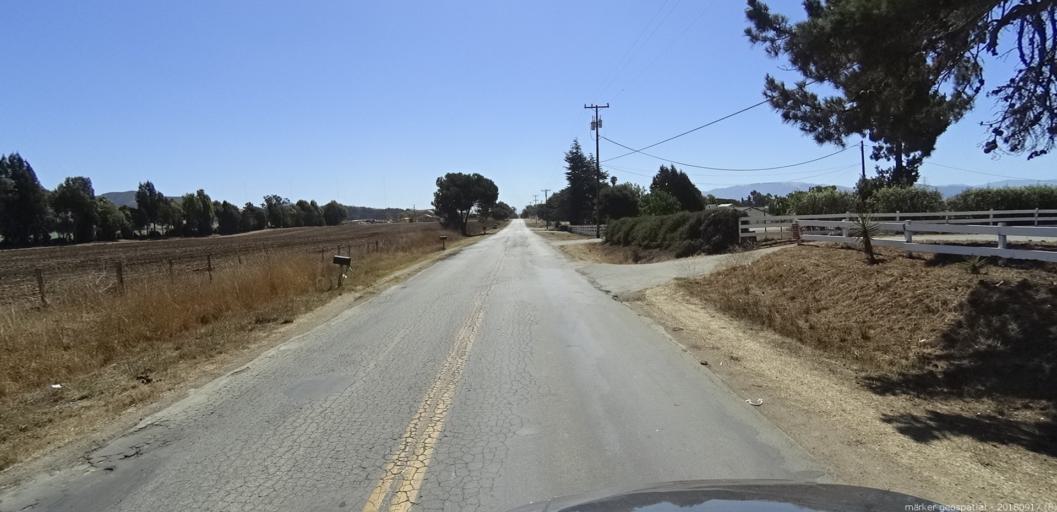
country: US
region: California
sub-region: Monterey County
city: Prunedale
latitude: 36.7385
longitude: -121.6006
